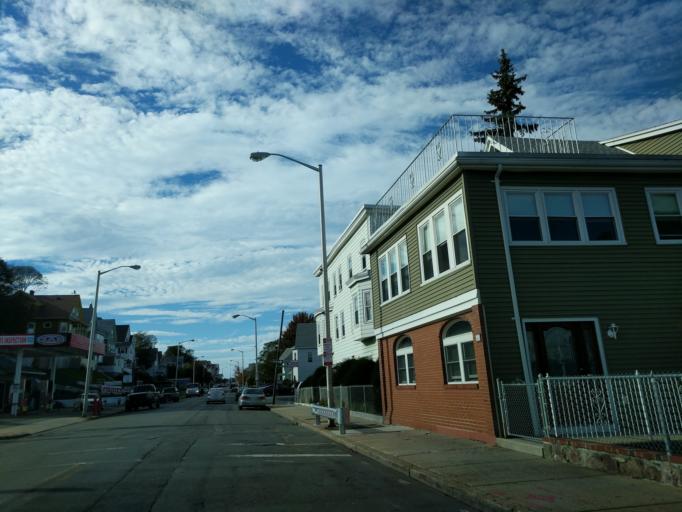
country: US
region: Massachusetts
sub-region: Middlesex County
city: Everett
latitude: 42.4182
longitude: -71.0510
